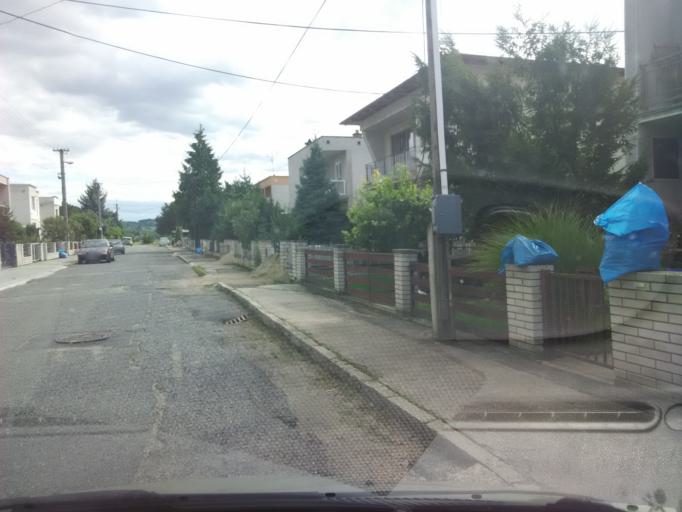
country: SK
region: Nitriansky
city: Levice
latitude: 48.2090
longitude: 18.6199
